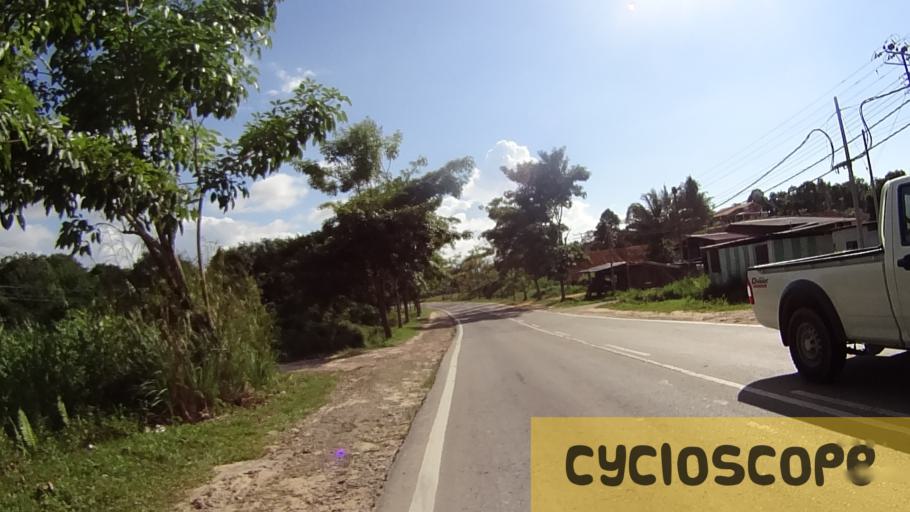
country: MY
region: Sabah
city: Beaufort
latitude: 5.0583
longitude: 115.5504
